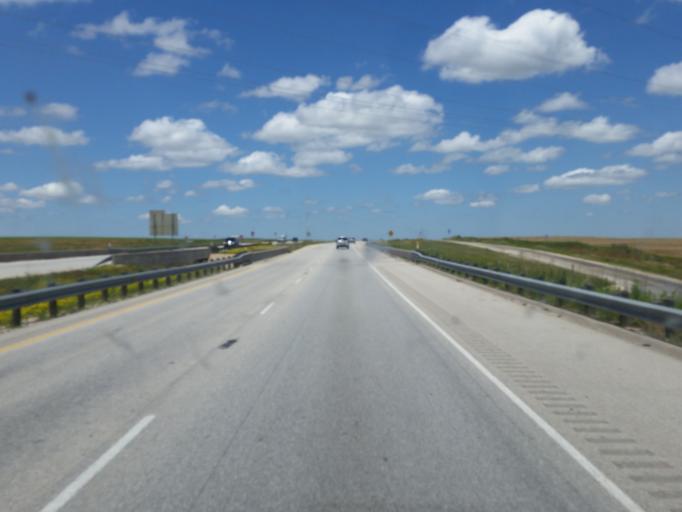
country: US
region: Texas
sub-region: Nolan County
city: Sweetwater
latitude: 32.4642
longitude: -100.3827
